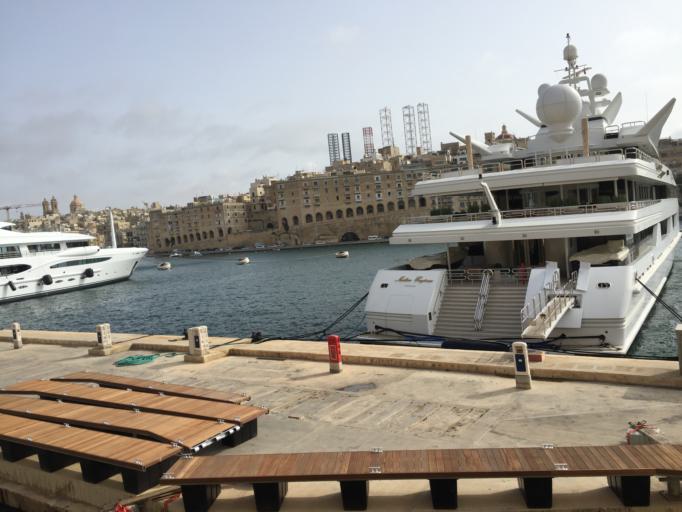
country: MT
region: Il-Birgu
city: Vittoriosa
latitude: 35.8920
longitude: 14.5173
